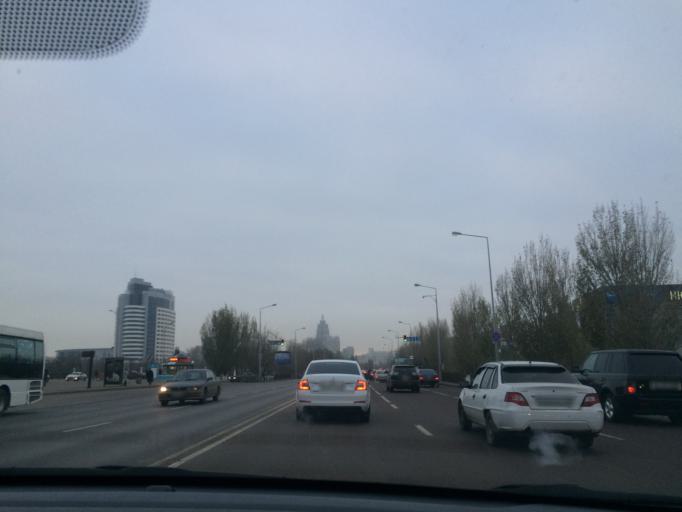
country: KZ
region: Astana Qalasy
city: Astana
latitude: 51.1537
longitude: 71.4124
